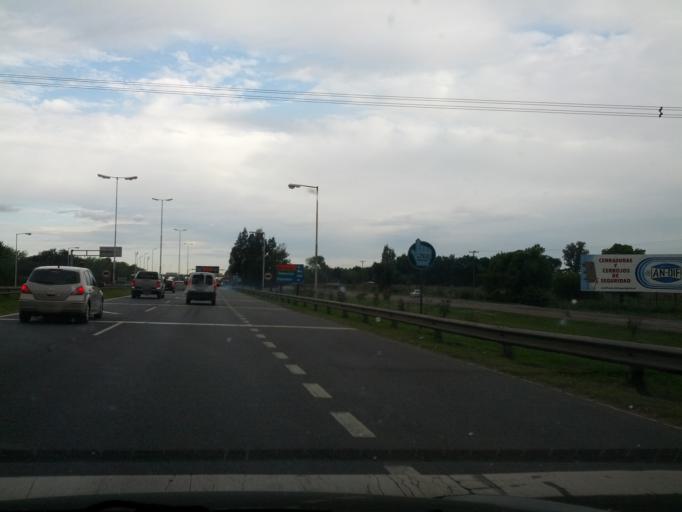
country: AR
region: Buenos Aires
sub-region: Partido de General Rodriguez
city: General Rodriguez
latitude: -34.5787
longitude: -59.0128
